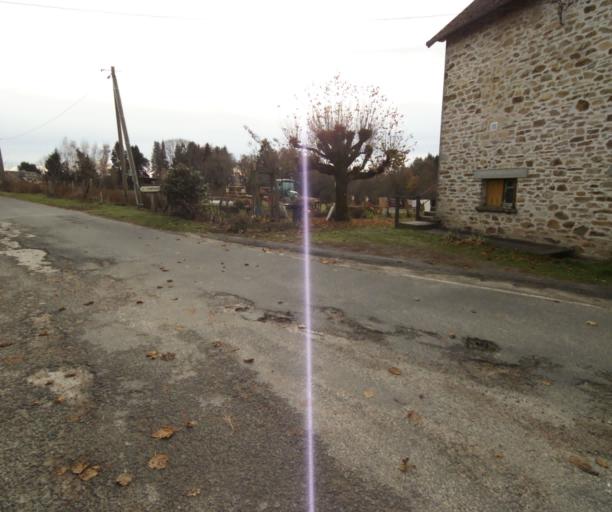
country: FR
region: Limousin
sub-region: Departement de la Correze
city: Saint-Mexant
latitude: 45.2634
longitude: 1.6460
